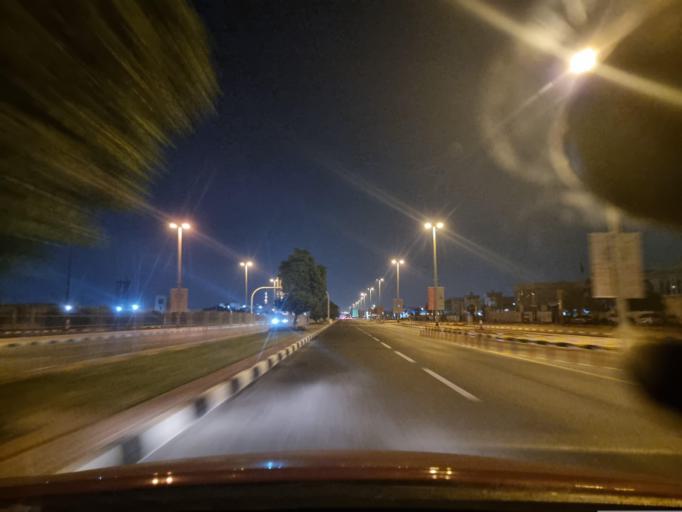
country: AE
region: Ash Shariqah
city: Sharjah
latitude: 25.3556
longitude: 55.4485
